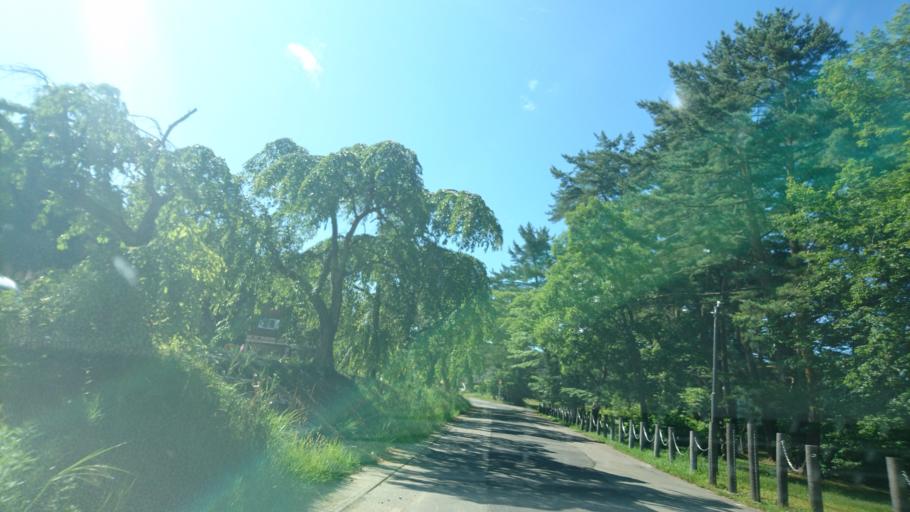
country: JP
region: Akita
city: Kakunodatemachi
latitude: 39.7337
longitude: 140.6979
